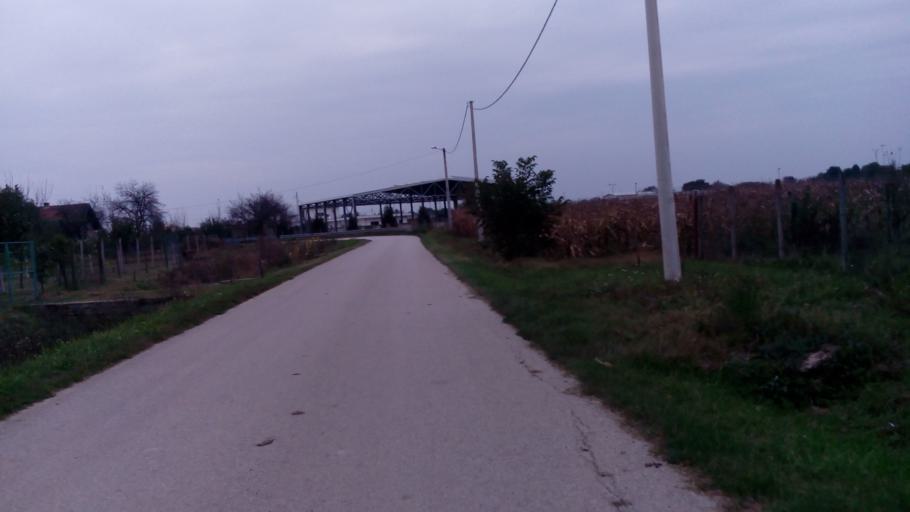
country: HR
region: Vukovarsko-Srijemska
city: Vinkovci
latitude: 45.2717
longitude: 18.8126
